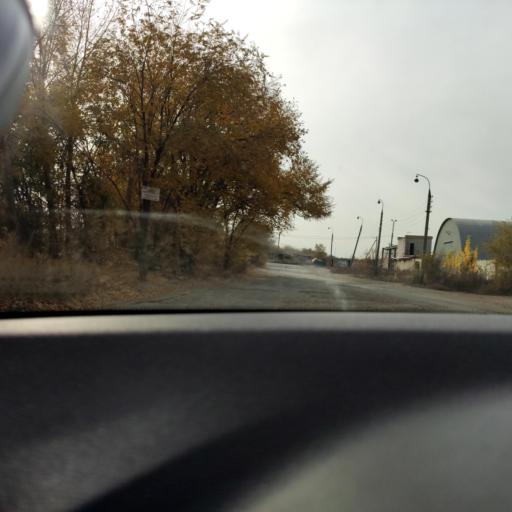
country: RU
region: Samara
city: Samara
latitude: 53.1858
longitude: 50.2309
